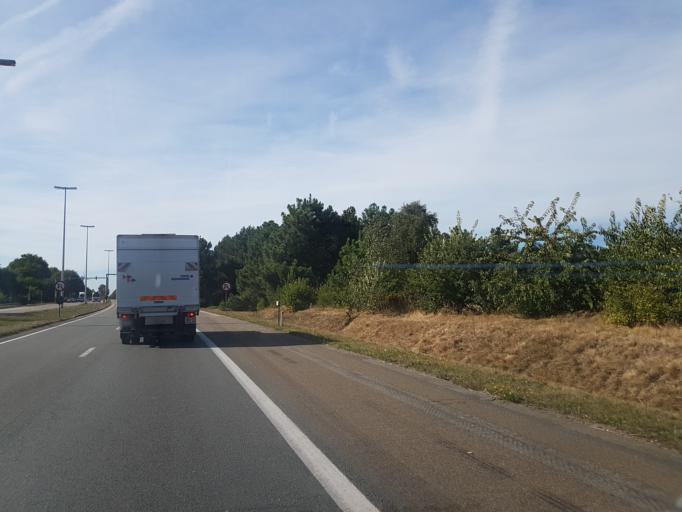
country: BE
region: Flanders
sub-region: Provincie Limburg
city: Lommel
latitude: 51.2235
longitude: 5.2940
